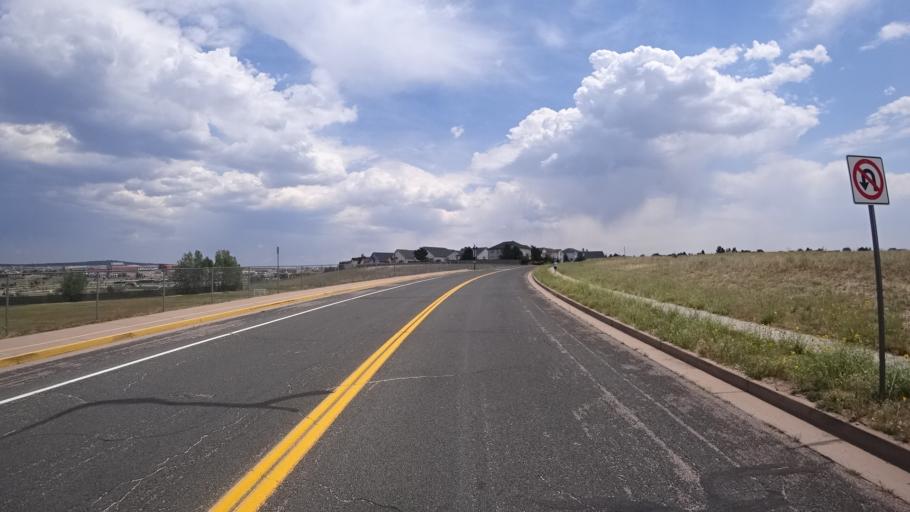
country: US
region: Colorado
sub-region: El Paso County
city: Black Forest
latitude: 38.9619
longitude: -104.7648
